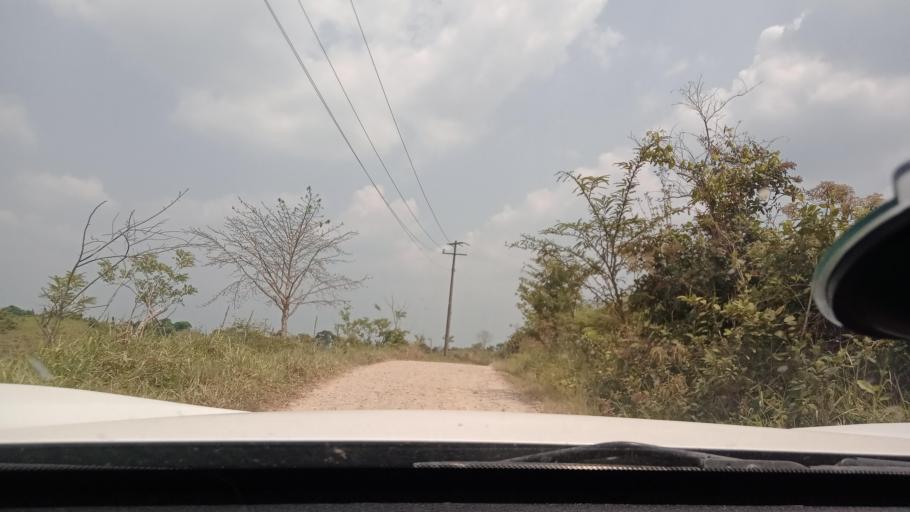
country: MX
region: Tabasco
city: Chontalpa
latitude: 17.5796
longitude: -93.6982
